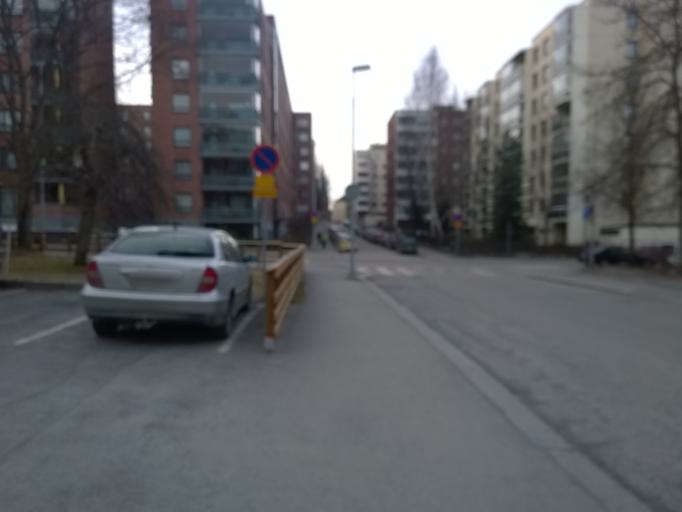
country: FI
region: Pirkanmaa
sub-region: Tampere
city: Tampere
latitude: 61.4929
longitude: 23.7510
